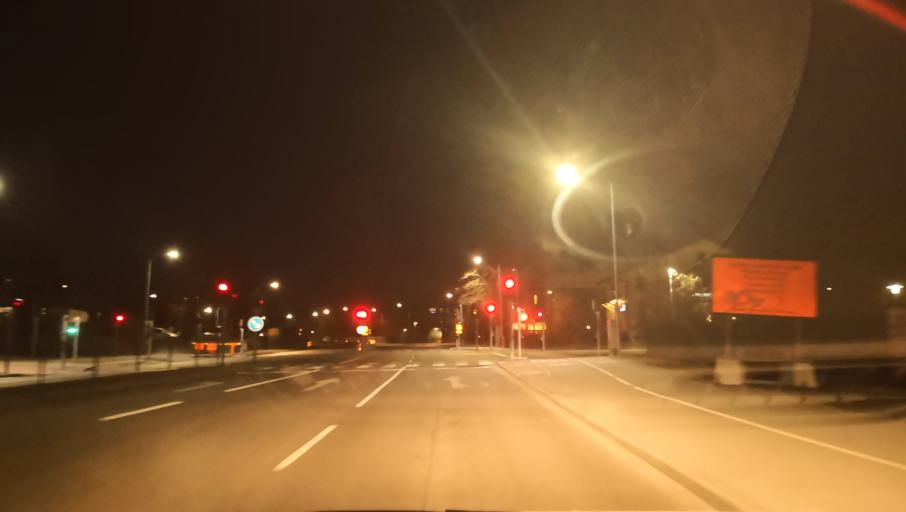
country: SE
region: Stockholm
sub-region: Nacka Kommun
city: Nacka
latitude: 59.3073
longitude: 18.1576
